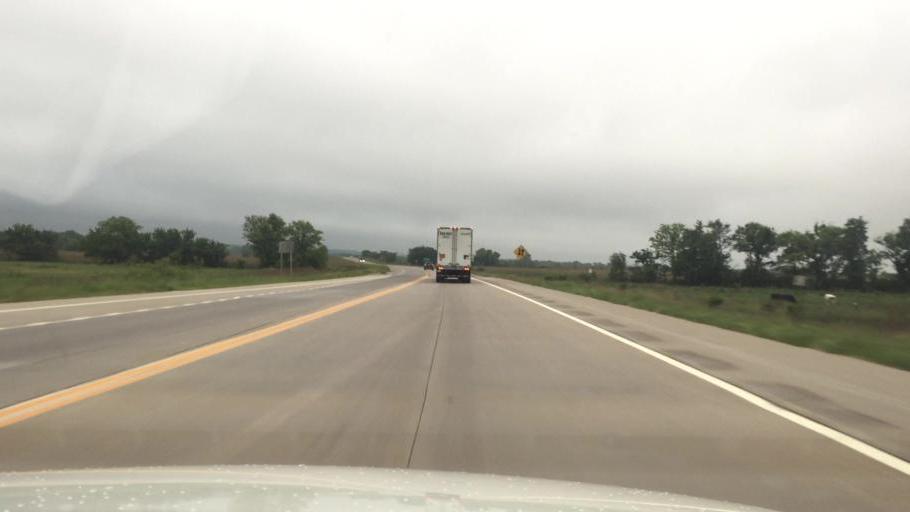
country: US
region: Kansas
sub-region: Montgomery County
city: Cherryvale
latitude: 37.2071
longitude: -95.5850
